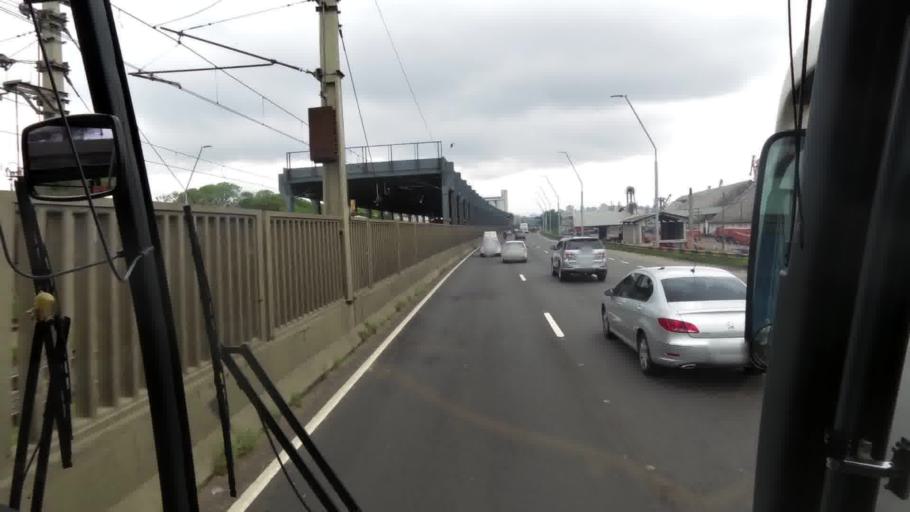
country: BR
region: Rio Grande do Sul
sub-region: Porto Alegre
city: Porto Alegre
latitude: -30.0050
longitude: -51.2090
